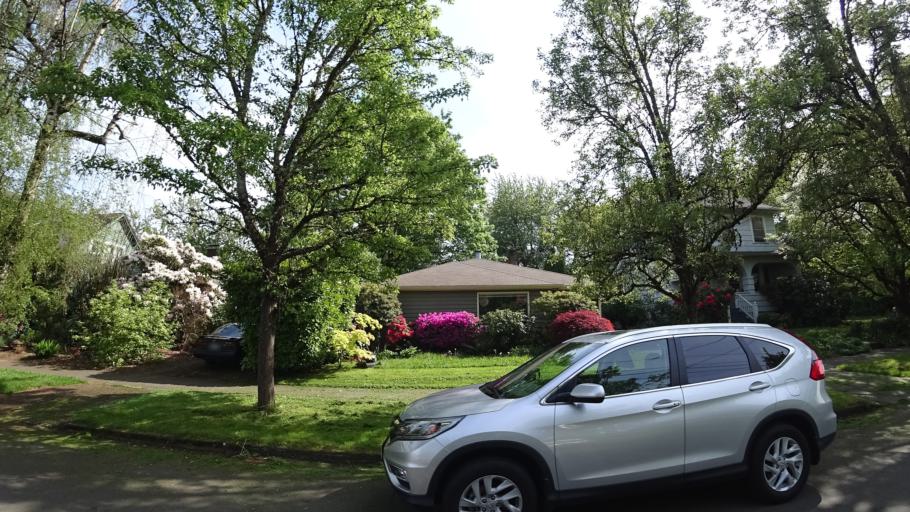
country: US
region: Oregon
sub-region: Clackamas County
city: Milwaukie
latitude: 45.4807
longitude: -122.6190
